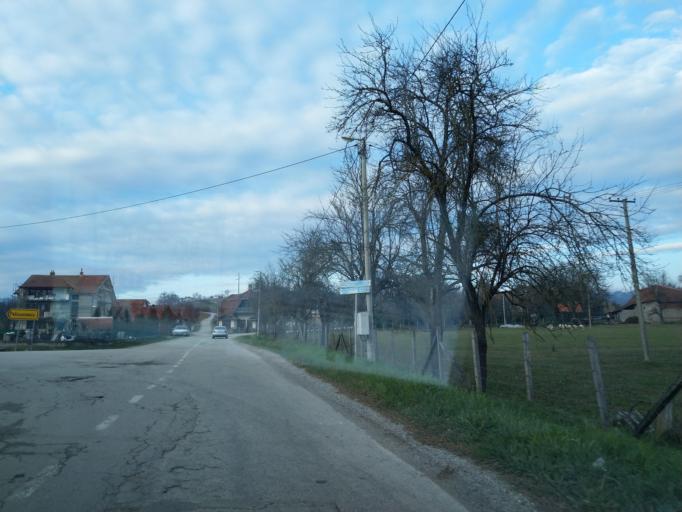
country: RS
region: Central Serbia
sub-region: Zlatiborski Okrug
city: Kosjeric
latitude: 43.9295
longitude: 19.8976
